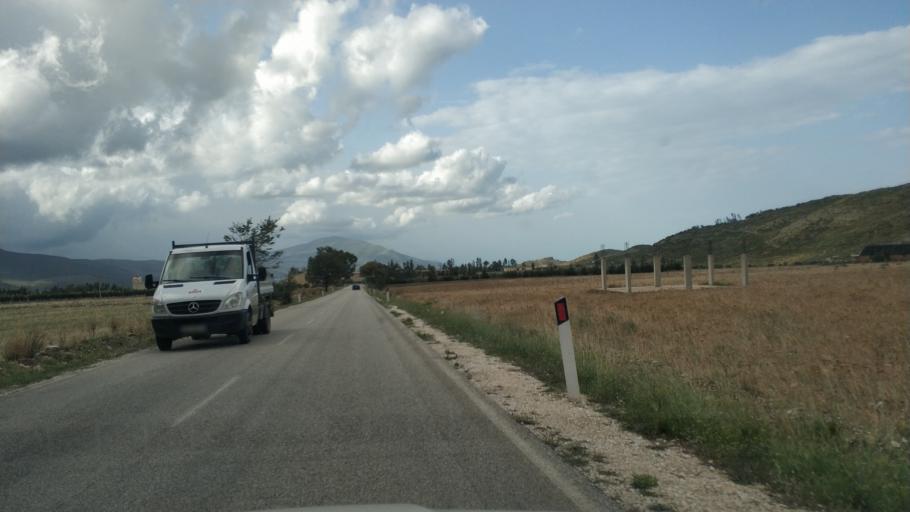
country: AL
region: Vlore
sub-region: Rrethi i Vlores
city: Orikum
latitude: 40.2761
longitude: 19.5070
